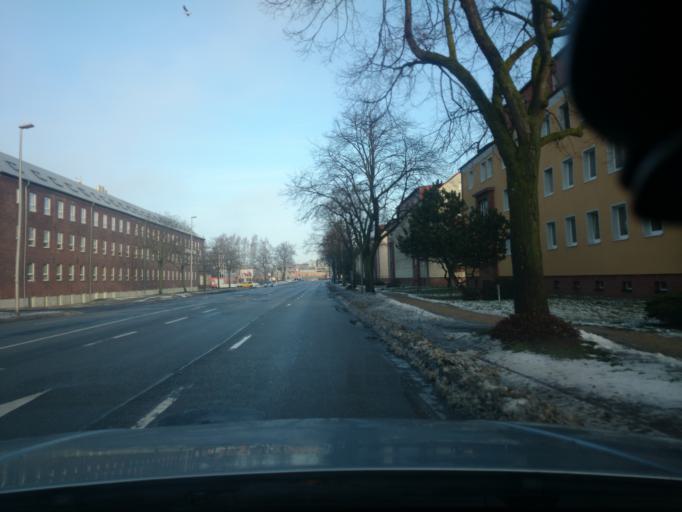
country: DE
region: Mecklenburg-Vorpommern
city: Stralsund
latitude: 54.3091
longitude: 13.0687
